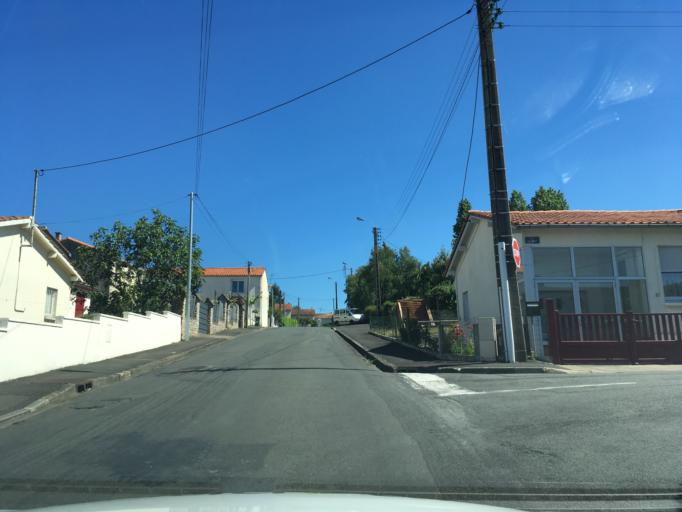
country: FR
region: Poitou-Charentes
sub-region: Departement des Deux-Sevres
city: Niort
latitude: 46.3230
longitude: -0.4358
